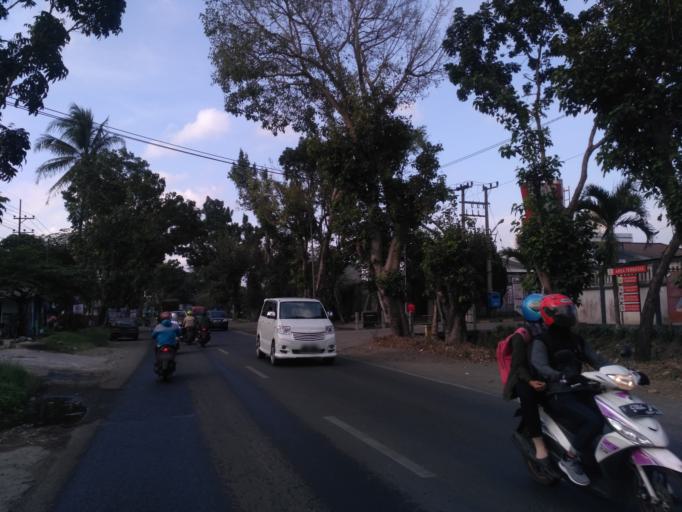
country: ID
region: East Java
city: Wadung
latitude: -8.0390
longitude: 112.6099
